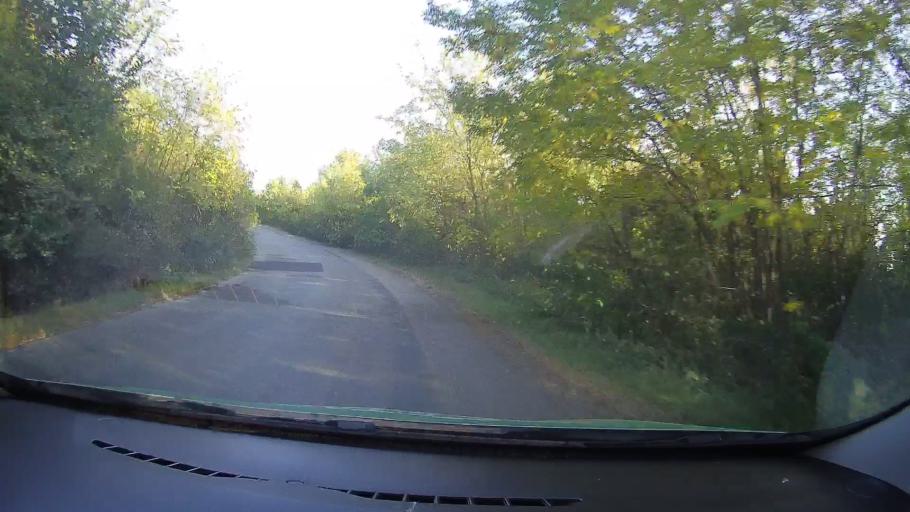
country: RO
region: Arad
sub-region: Comuna Silindia
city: Silindia
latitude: 46.3291
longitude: 21.9423
